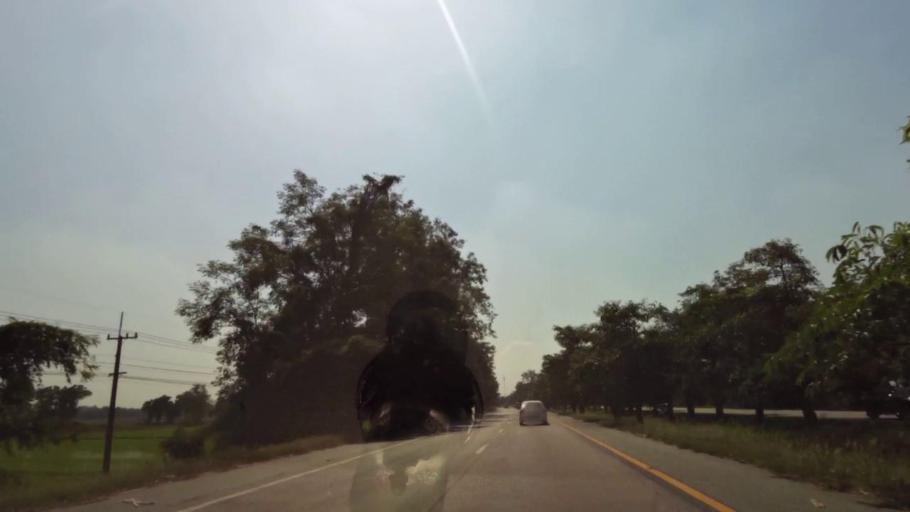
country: TH
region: Phitsanulok
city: Bang Rakam
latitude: 16.6455
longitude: 100.1503
